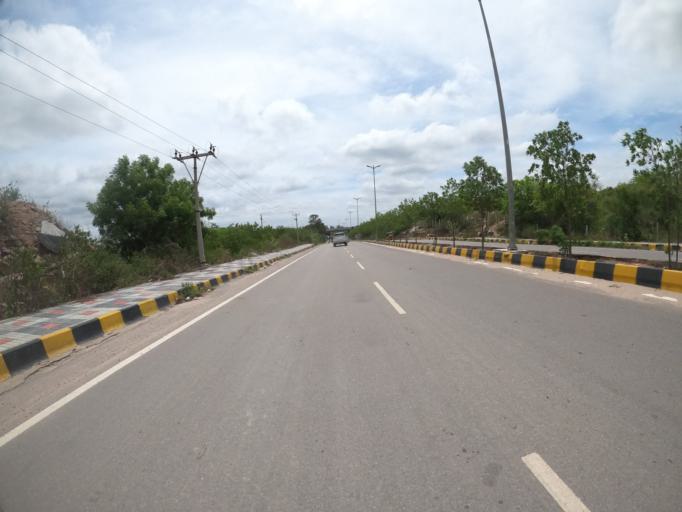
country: IN
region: Telangana
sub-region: Hyderabad
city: Hyderabad
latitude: 17.3214
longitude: 78.3721
